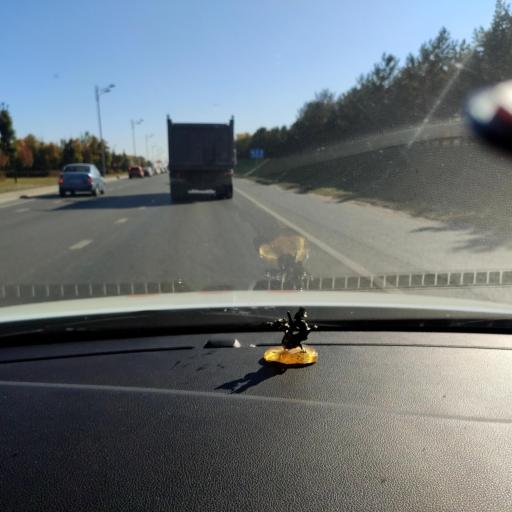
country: RU
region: Tatarstan
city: Stolbishchi
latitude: 55.7226
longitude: 49.1976
